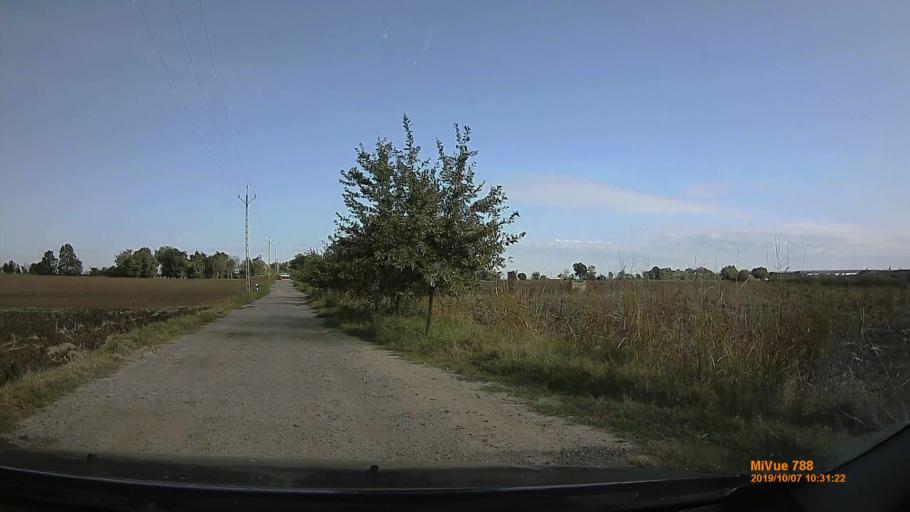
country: HU
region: Bekes
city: Kondoros
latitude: 46.7460
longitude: 20.8447
